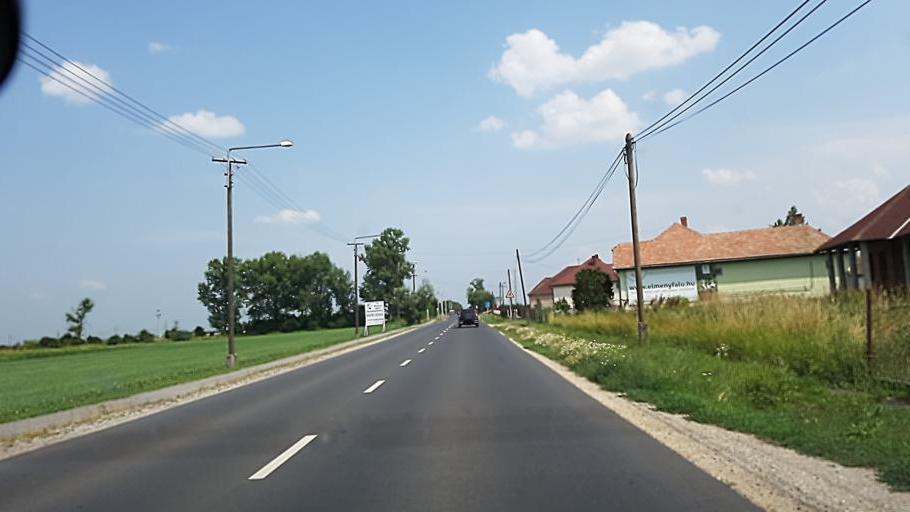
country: HU
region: Heves
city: Besenyotelek
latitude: 47.6931
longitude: 20.4425
